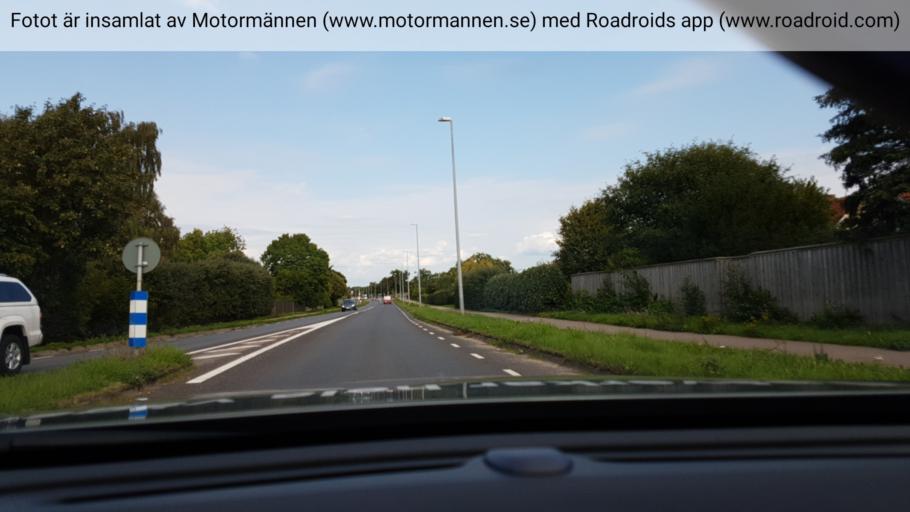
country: SE
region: Halland
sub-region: Halmstads Kommun
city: Mjallby
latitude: 56.6605
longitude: 12.8082
